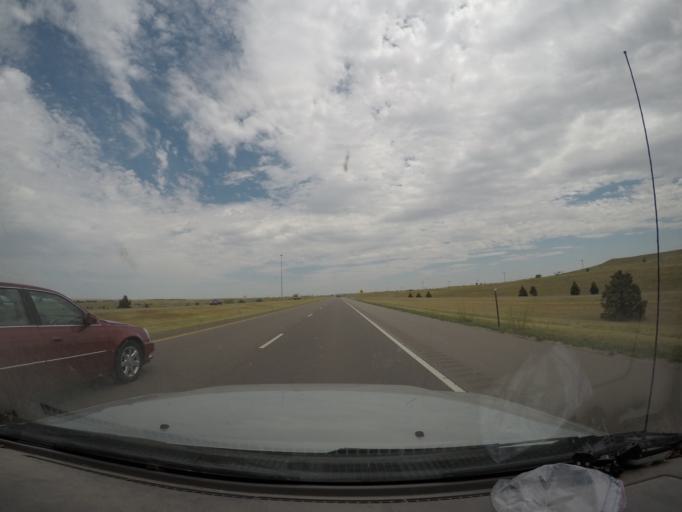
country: US
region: Nebraska
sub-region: Kimball County
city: Kimball
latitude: 41.2165
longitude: -103.6615
